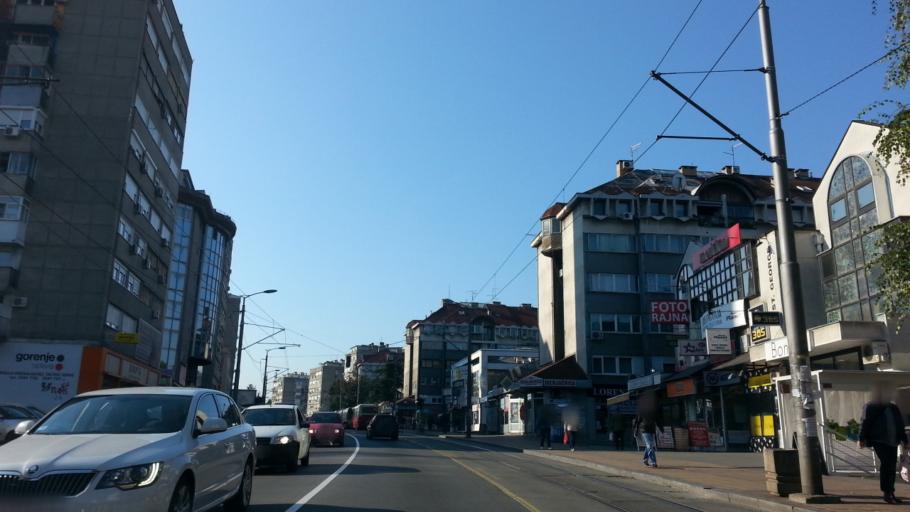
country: RS
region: Central Serbia
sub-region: Belgrade
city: Cukarica
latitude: 44.7765
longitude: 20.4138
